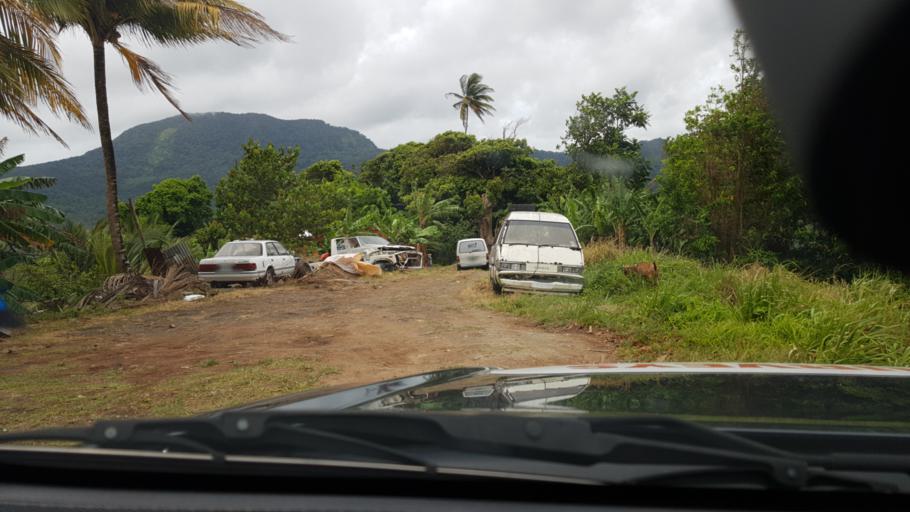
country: LC
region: Castries Quarter
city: Bisee
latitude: 14.0071
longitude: -60.9356
